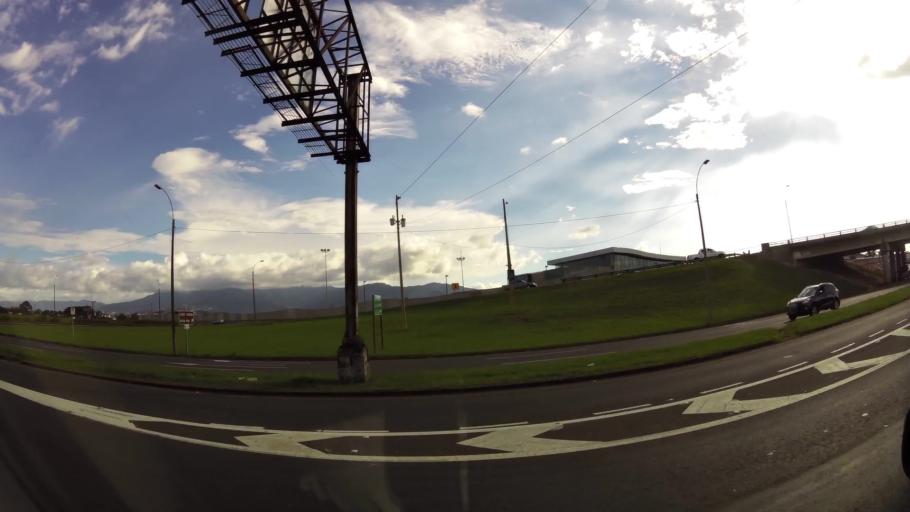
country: CR
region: Alajuela
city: Alajuela
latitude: 10.0000
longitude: -84.2014
